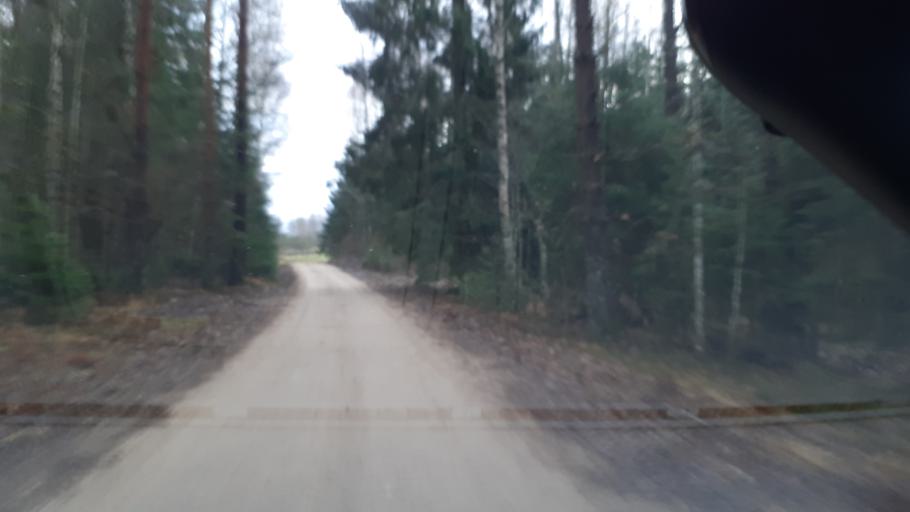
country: LV
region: Kuldigas Rajons
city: Kuldiga
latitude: 56.9007
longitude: 21.9131
